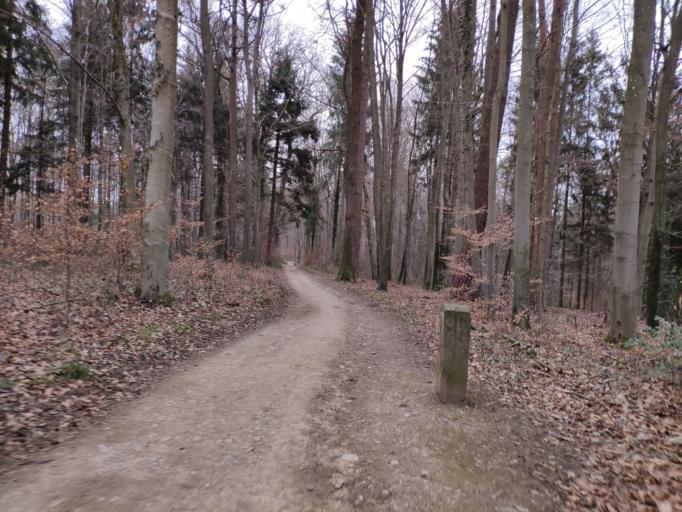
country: DE
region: Baden-Wuerttemberg
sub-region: Freiburg Region
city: Inzlingen
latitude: 47.5994
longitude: 7.6930
